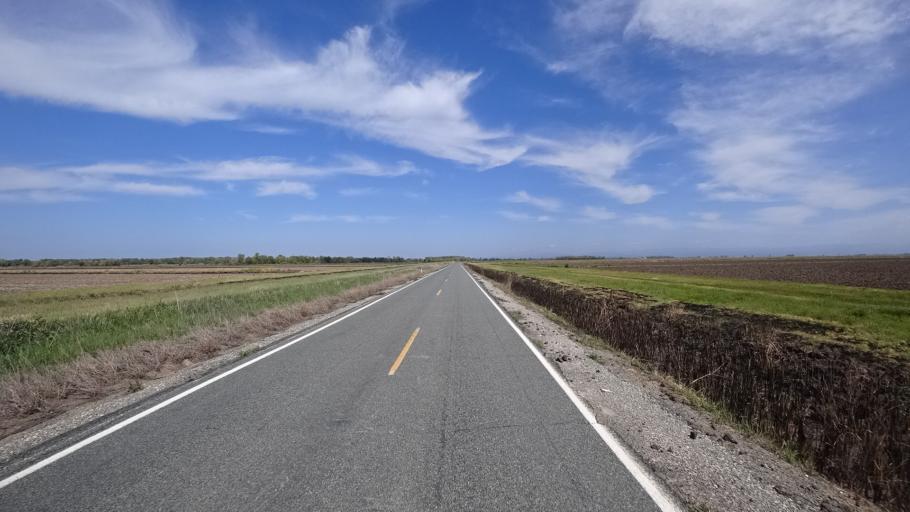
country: US
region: California
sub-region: Butte County
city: Durham
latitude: 39.5102
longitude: -121.8574
